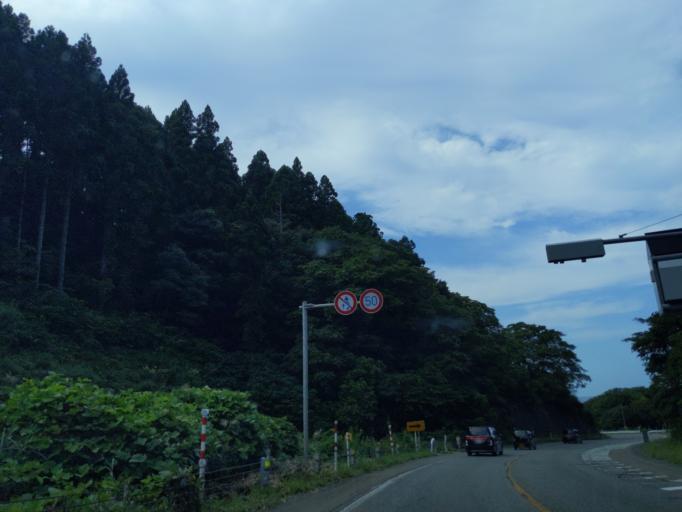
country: JP
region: Niigata
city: Kashiwazaki
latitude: 37.3193
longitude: 138.4413
